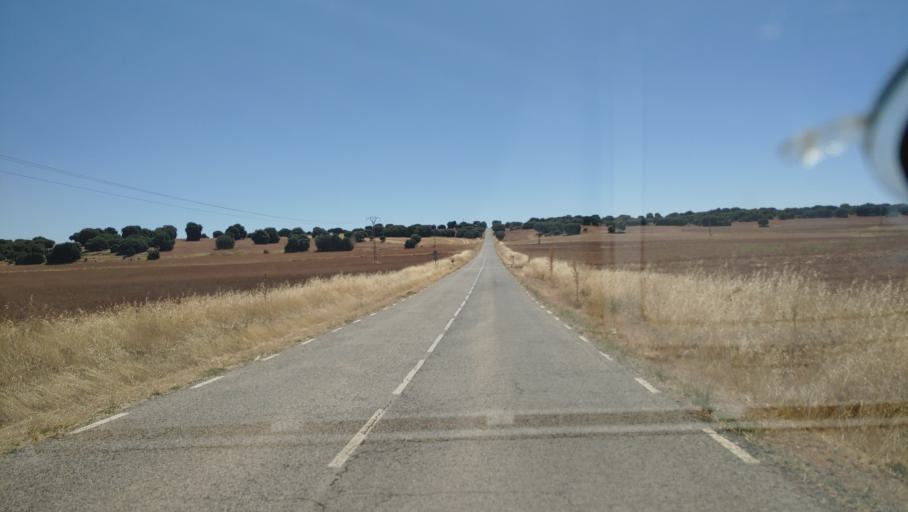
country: ES
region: Castille-La Mancha
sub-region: Provincia de Albacete
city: Ossa de Montiel
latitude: 38.9352
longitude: -2.7520
